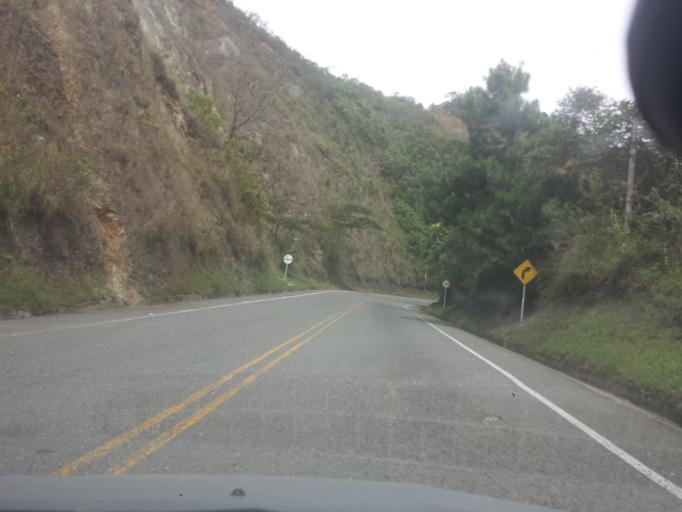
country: CO
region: Antioquia
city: Liborina
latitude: 6.6388
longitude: -75.8723
